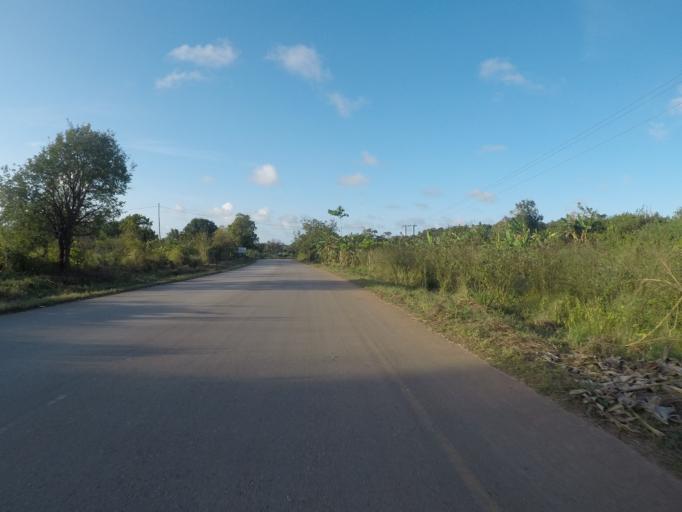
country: TZ
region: Zanzibar North
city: Kijini
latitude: -5.8331
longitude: 39.2911
